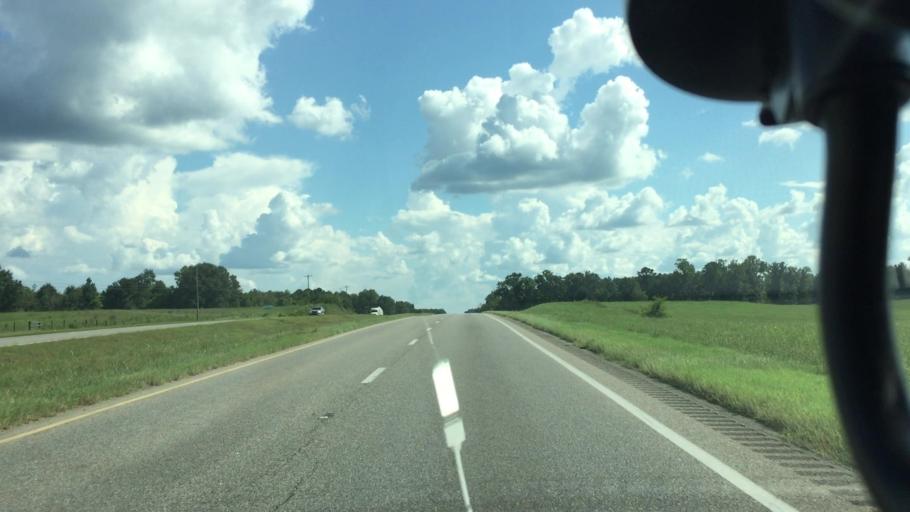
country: US
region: Alabama
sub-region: Montgomery County
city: Pike Road
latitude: 32.2184
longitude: -86.1180
